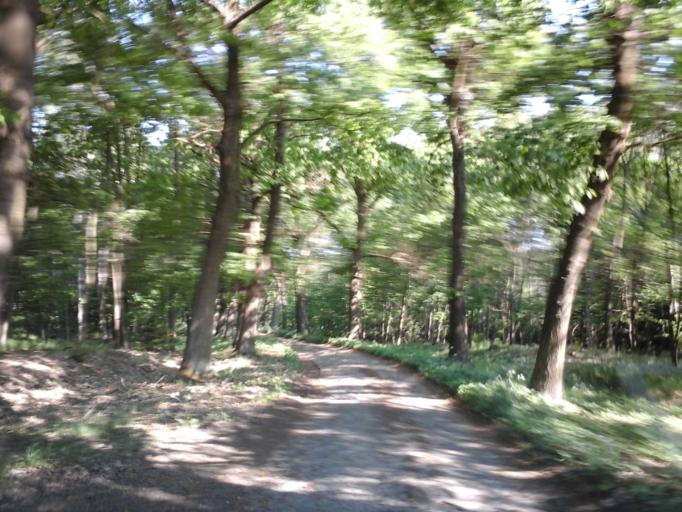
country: PL
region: West Pomeranian Voivodeship
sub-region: Powiat choszczenski
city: Recz
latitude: 53.3021
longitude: 15.5322
